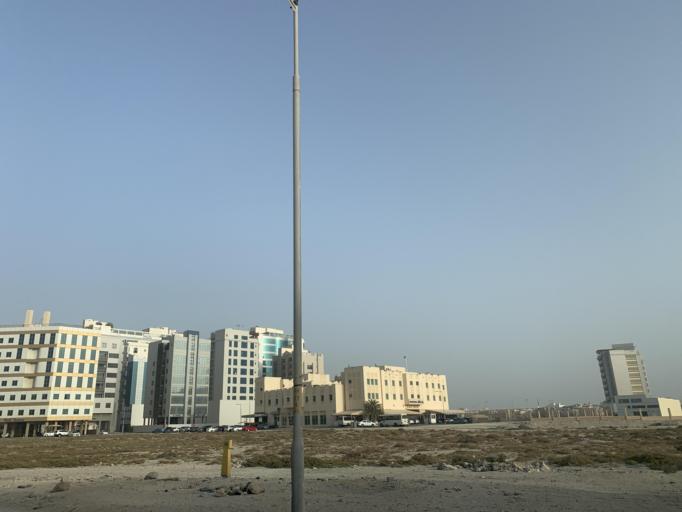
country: BH
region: Manama
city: Jidd Hafs
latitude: 26.2396
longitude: 50.5286
